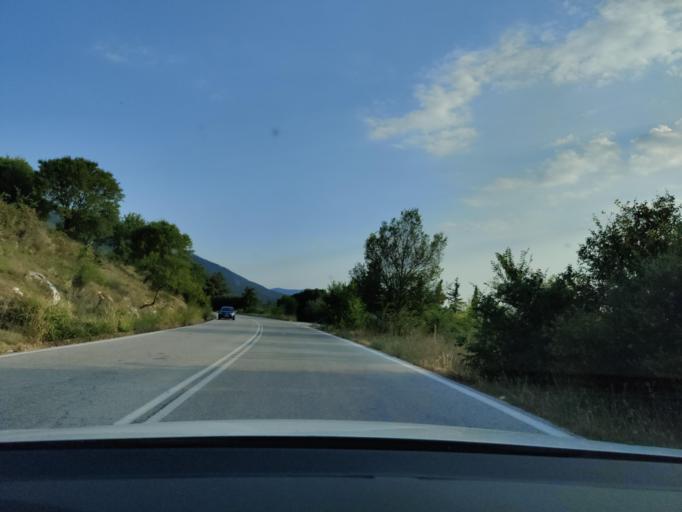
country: GR
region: East Macedonia and Thrace
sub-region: Nomos Kavalas
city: Zygos
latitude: 41.0029
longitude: 24.3803
